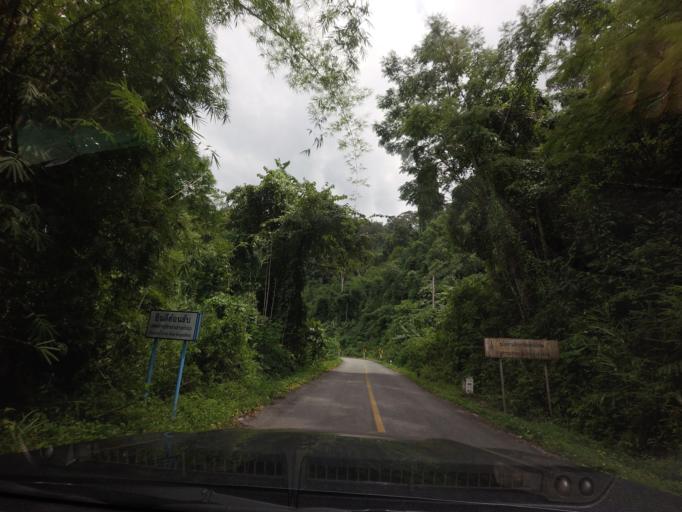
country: TH
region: Loei
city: Na Haeo
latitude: 17.7006
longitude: 100.9490
